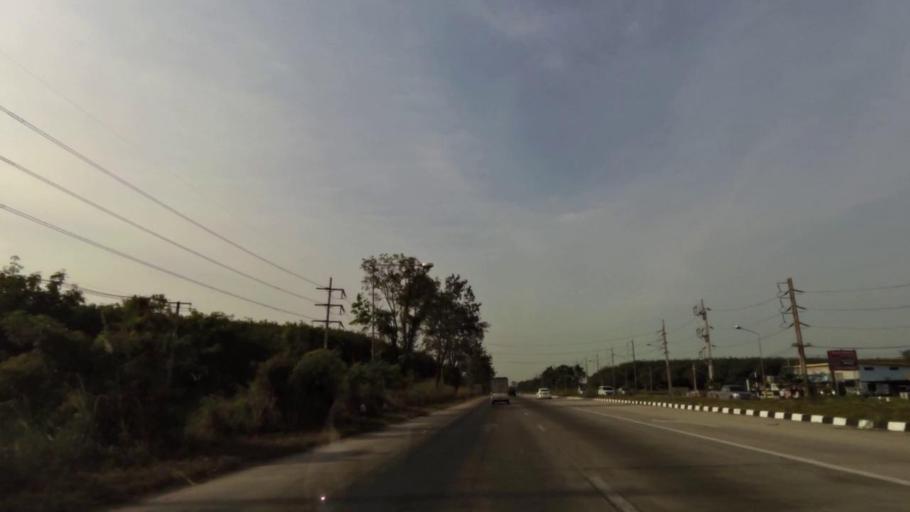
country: TH
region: Chon Buri
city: Ban Bueng
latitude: 13.2507
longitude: 101.2063
